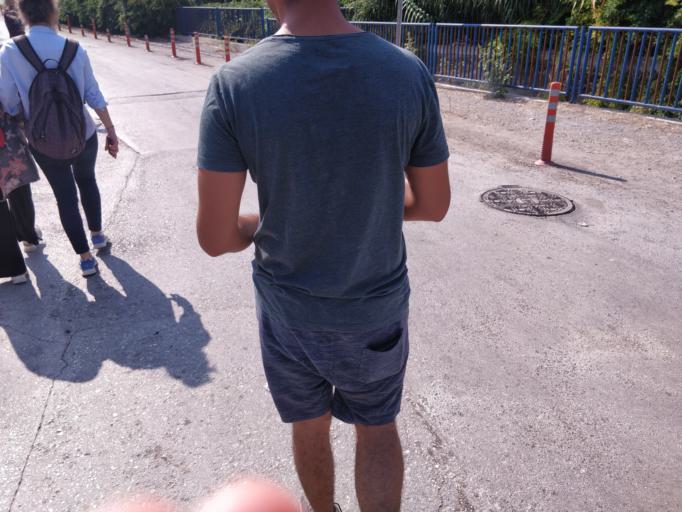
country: TR
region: Izmir
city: Urla
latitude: 38.3243
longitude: 26.7645
